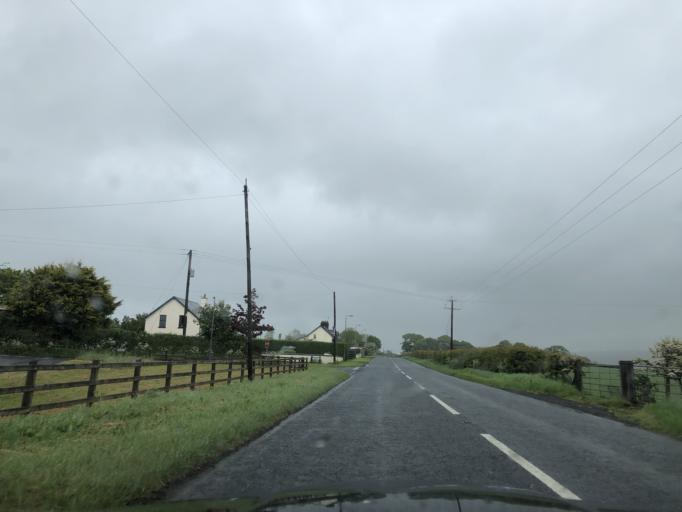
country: GB
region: Northern Ireland
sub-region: Moyle District
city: Ballycastle
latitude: 55.1827
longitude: -6.3145
